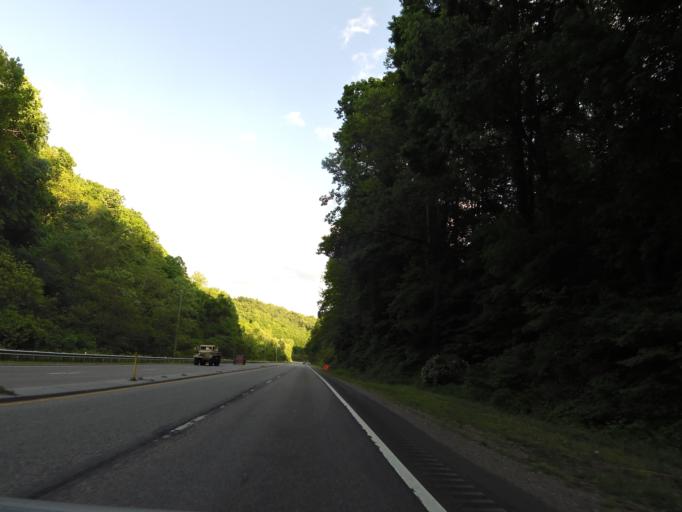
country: US
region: Virginia
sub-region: Washington County
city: Abingdon
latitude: 36.7621
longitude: -82.0640
